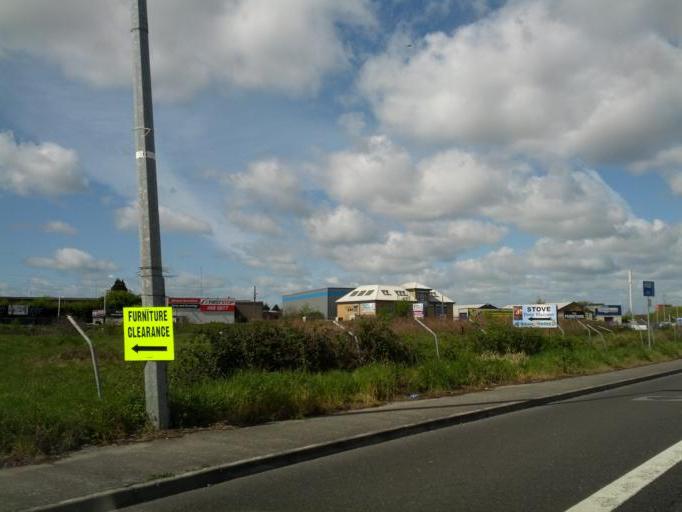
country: IE
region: Leinster
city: Ballyfermot
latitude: 53.3250
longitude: -6.3556
